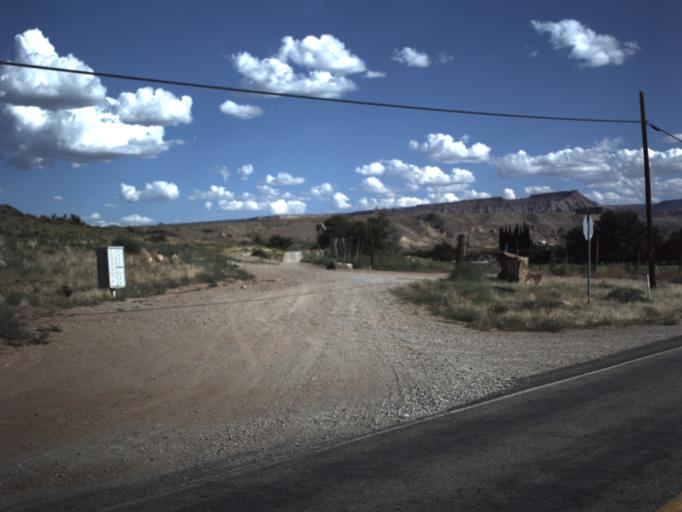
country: US
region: Utah
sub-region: Washington County
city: Toquerville
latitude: 37.2387
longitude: -113.2809
